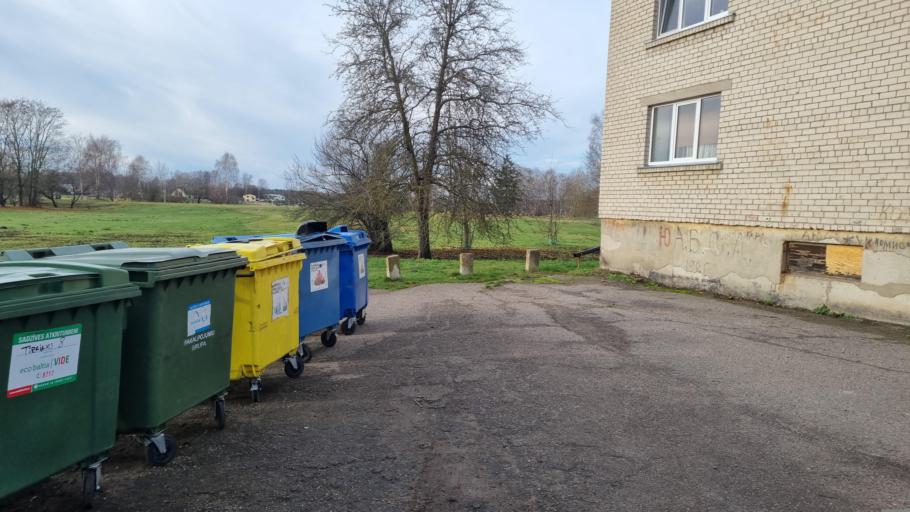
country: LV
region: Marupe
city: Marupe
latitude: 56.8808
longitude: 24.0656
